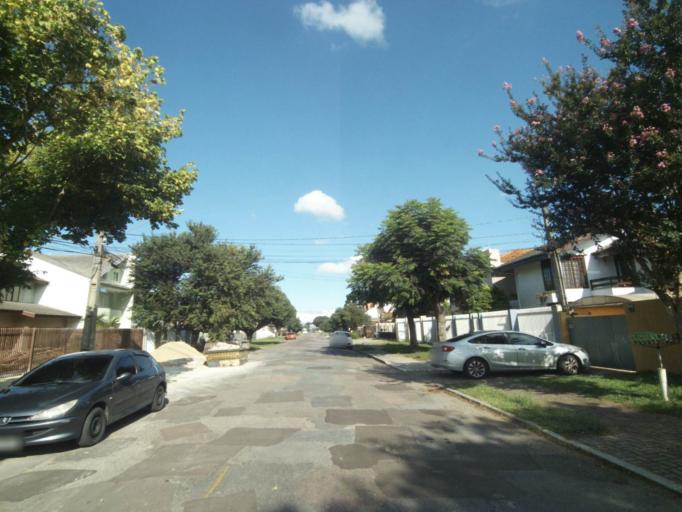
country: BR
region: Parana
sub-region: Pinhais
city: Pinhais
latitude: -25.4336
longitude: -49.2169
